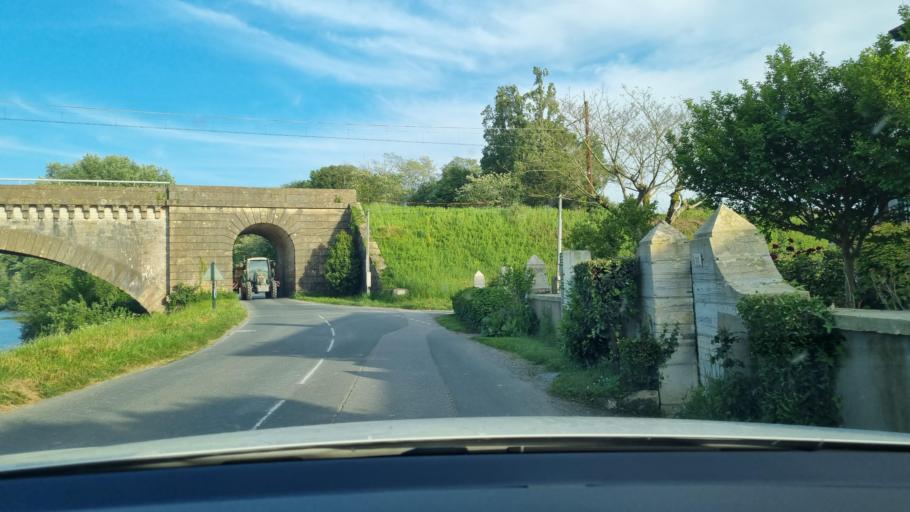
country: FR
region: Aquitaine
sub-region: Departement des Landes
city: Peyrehorade
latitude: 43.5381
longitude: -1.1597
